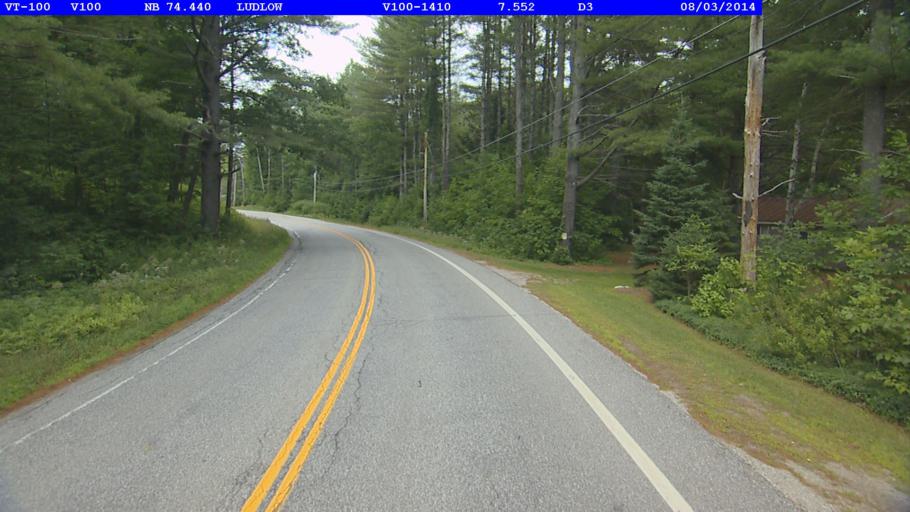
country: US
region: Vermont
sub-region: Windsor County
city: Chester
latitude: 43.4517
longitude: -72.7061
